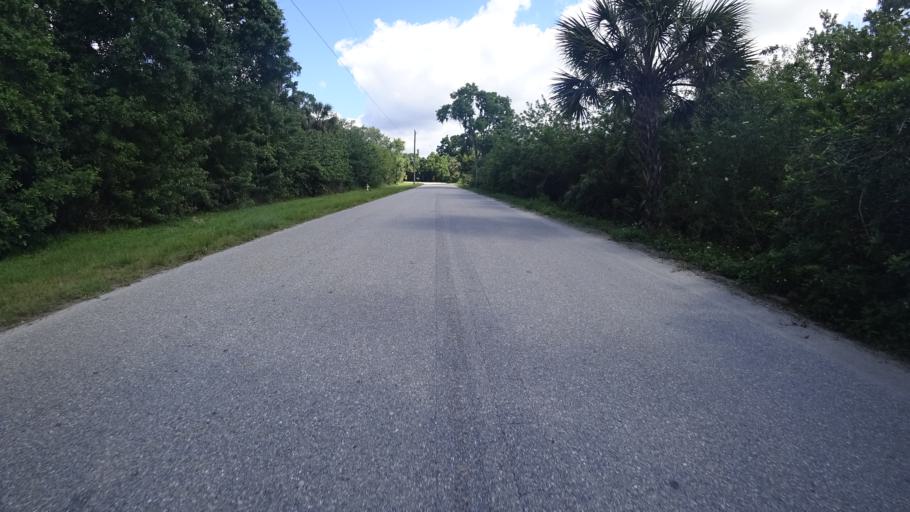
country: US
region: Florida
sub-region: Sarasota County
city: North Sarasota
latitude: 27.4101
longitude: -82.5283
